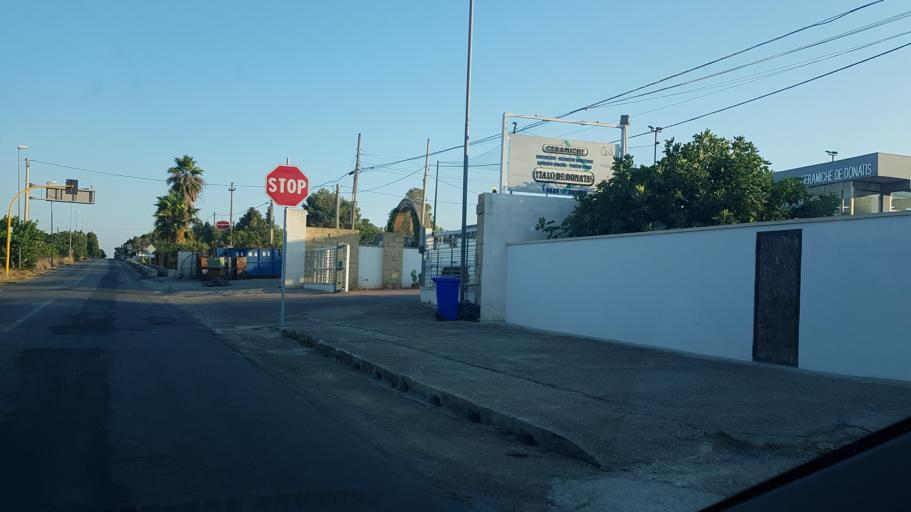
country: IT
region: Apulia
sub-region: Provincia di Lecce
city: Ruffano
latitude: 39.9731
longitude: 18.2546
